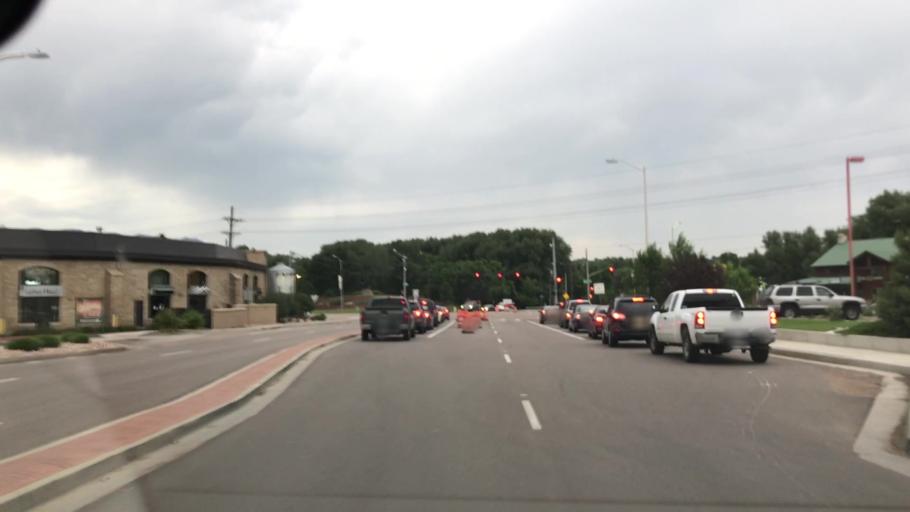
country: US
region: Colorado
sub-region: El Paso County
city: Colorado Springs
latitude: 38.8394
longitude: -104.8591
